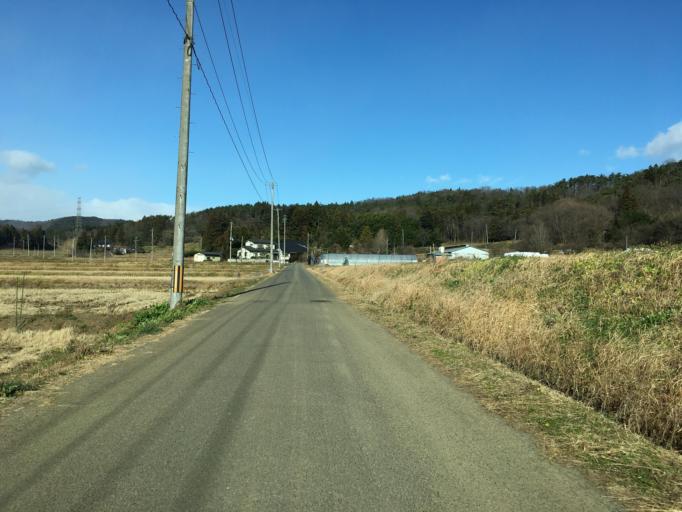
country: JP
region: Fukushima
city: Nihommatsu
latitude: 37.5817
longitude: 140.3957
